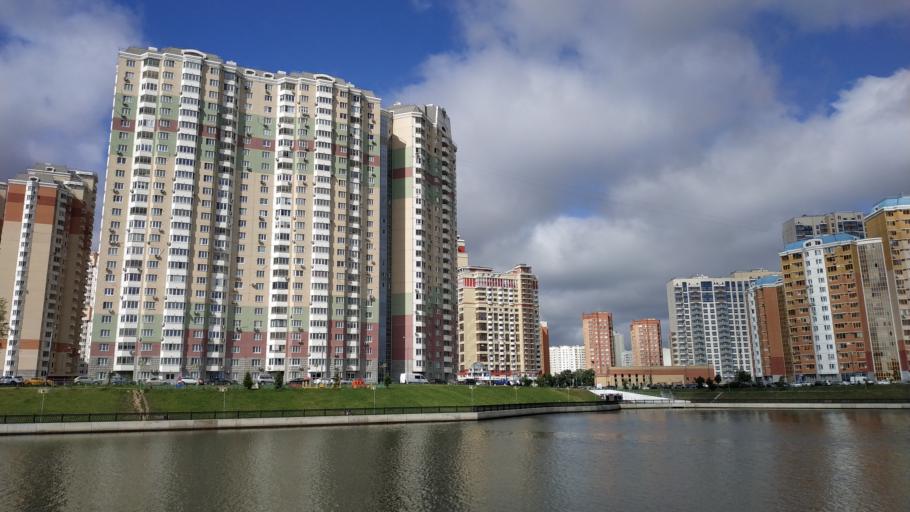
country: RU
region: Moskovskaya
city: Pavshino
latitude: 55.8244
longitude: 37.3802
